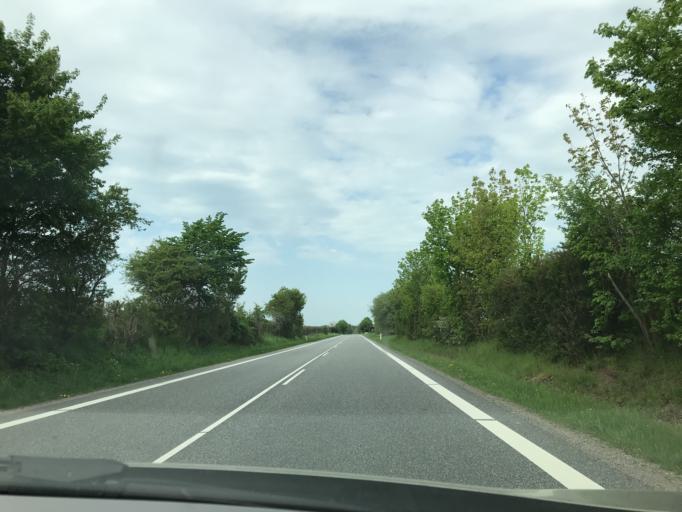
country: DK
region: South Denmark
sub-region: Assens Kommune
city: Assens
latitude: 55.3143
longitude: 9.9403
